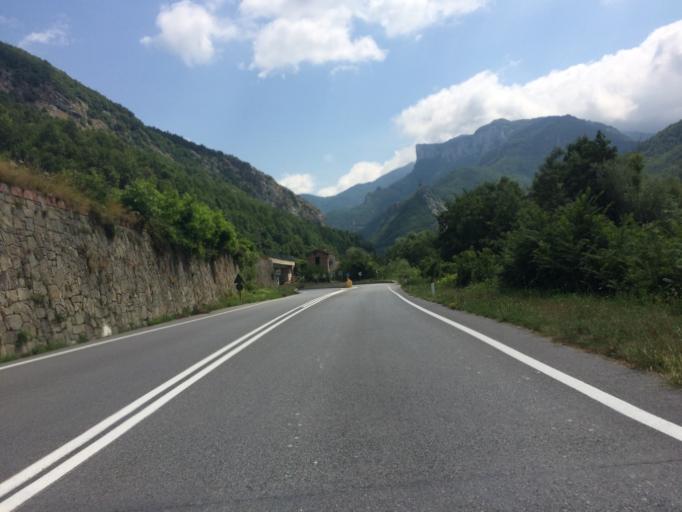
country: IT
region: Piedmont
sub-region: Provincia di Cuneo
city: Ormea
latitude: 44.1578
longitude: 7.9433
